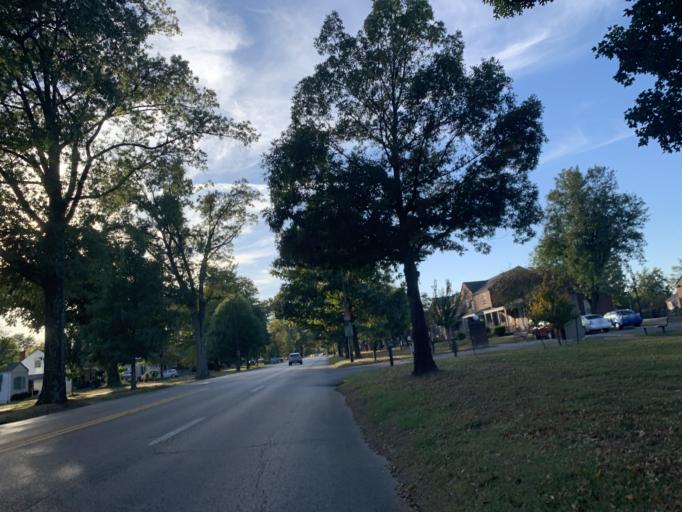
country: US
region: Kentucky
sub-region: Jefferson County
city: Shively
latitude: 38.2229
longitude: -85.7885
